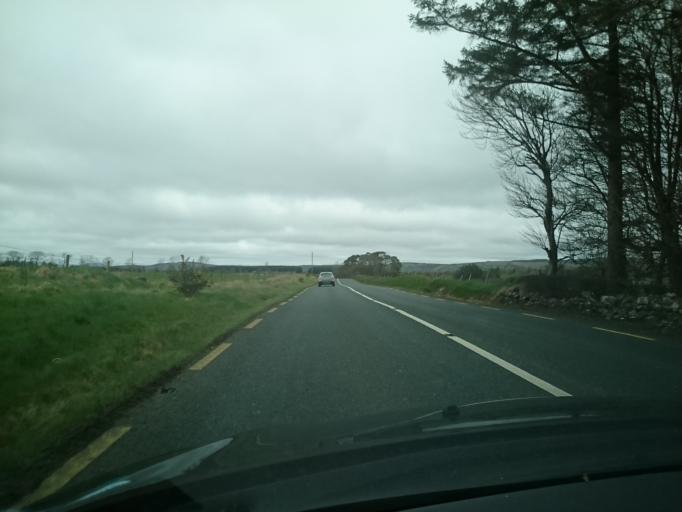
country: IE
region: Connaught
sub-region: Maigh Eo
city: Kiltamagh
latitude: 53.7850
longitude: -9.0827
